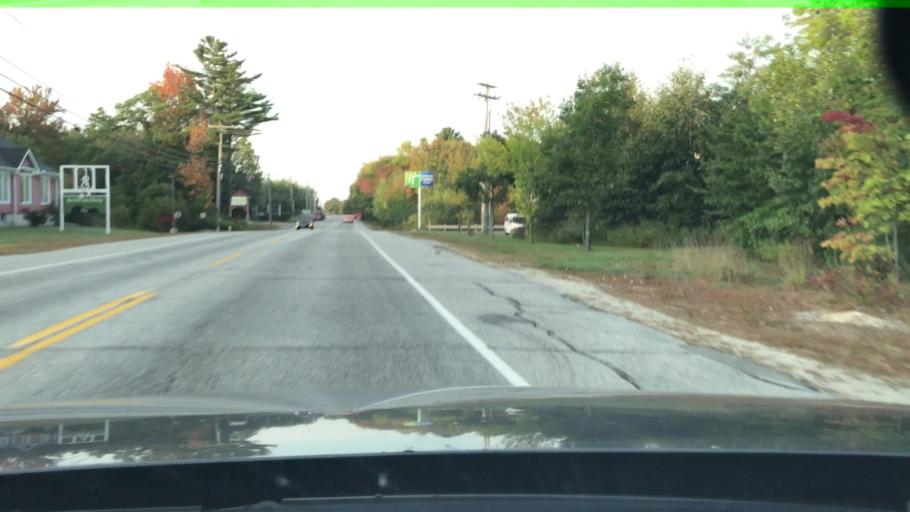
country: US
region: Maine
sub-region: Cumberland County
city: Freeport
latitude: 43.8364
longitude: -70.1255
